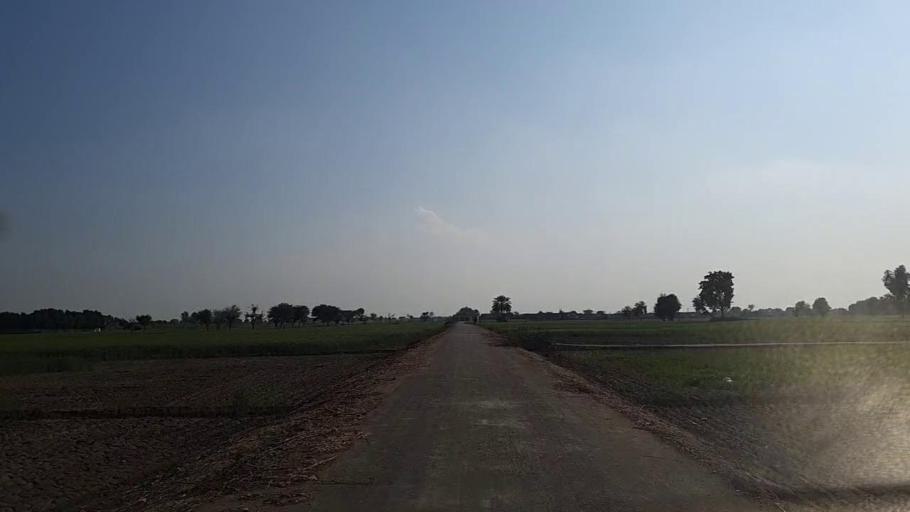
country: PK
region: Sindh
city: Jam Sahib
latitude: 26.2828
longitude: 68.6137
